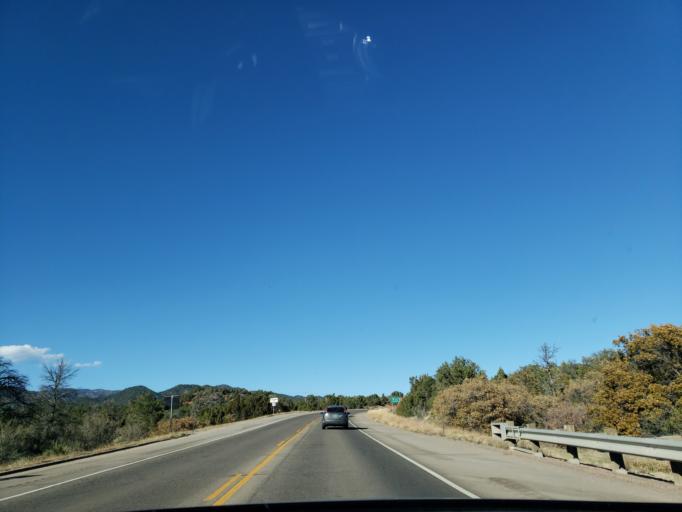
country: US
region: Colorado
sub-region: Fremont County
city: Penrose
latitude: 38.5661
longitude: -104.9429
